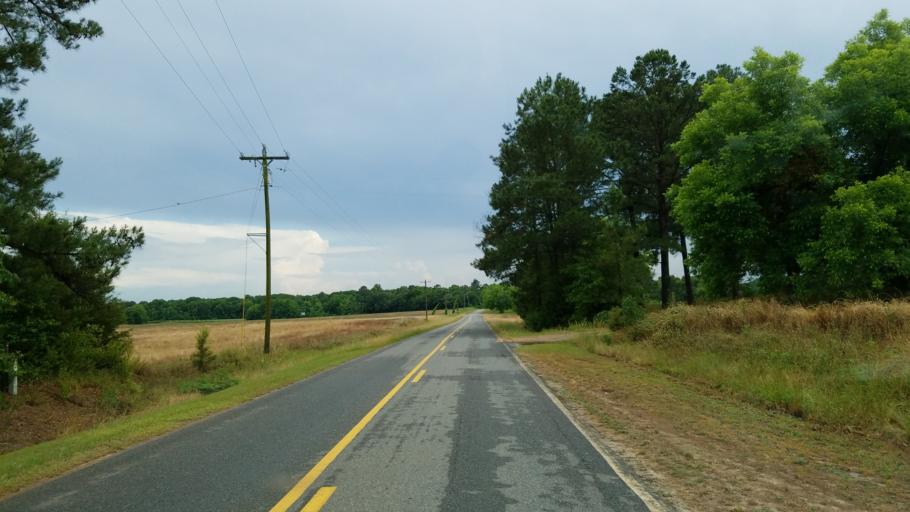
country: US
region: Georgia
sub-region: Dooly County
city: Unadilla
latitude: 32.2397
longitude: -83.7974
